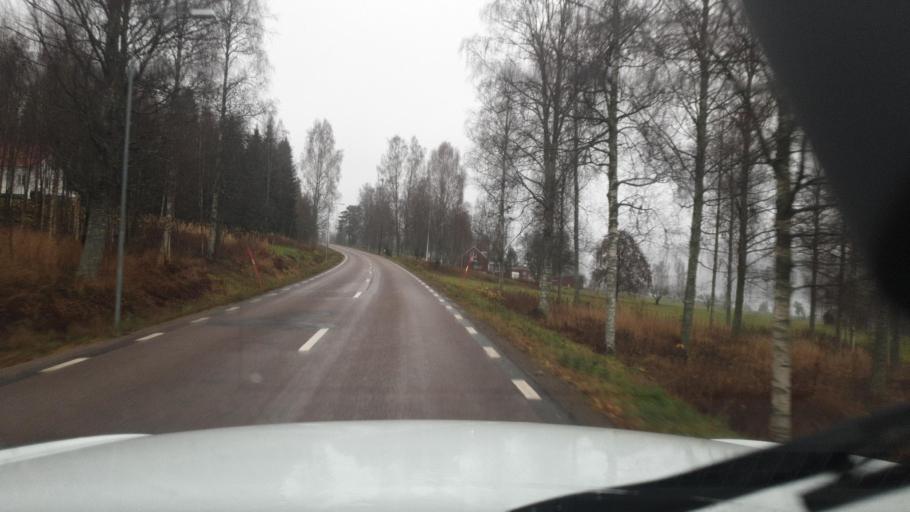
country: SE
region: Vaermland
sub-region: Sunne Kommun
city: Sunne
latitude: 59.8667
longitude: 12.9441
